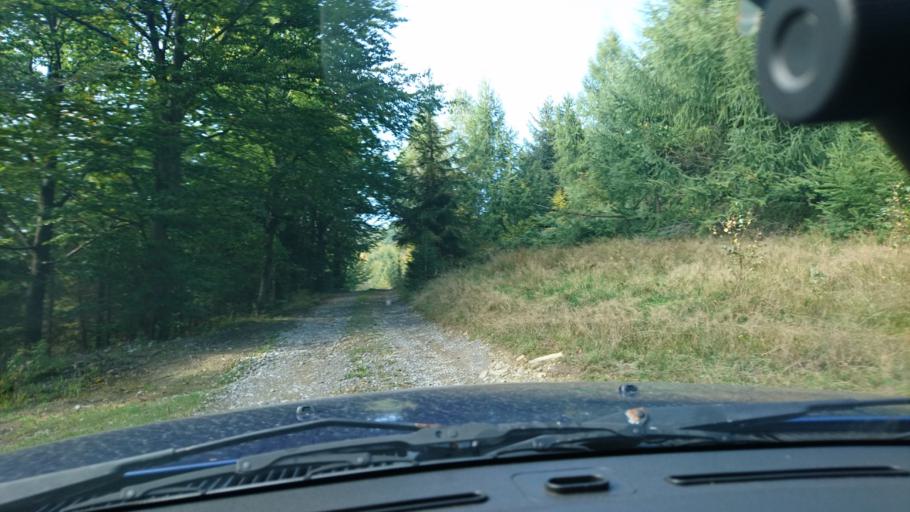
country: PL
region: Silesian Voivodeship
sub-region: Powiat bielski
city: Wilkowice
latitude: 49.7739
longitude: 19.1254
